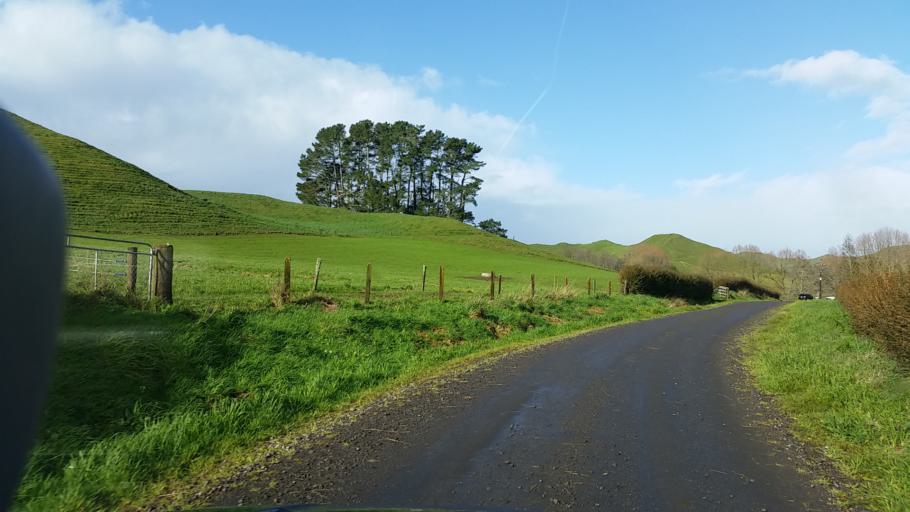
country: NZ
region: Taranaki
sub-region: South Taranaki District
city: Eltham
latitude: -39.3463
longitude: 174.4431
